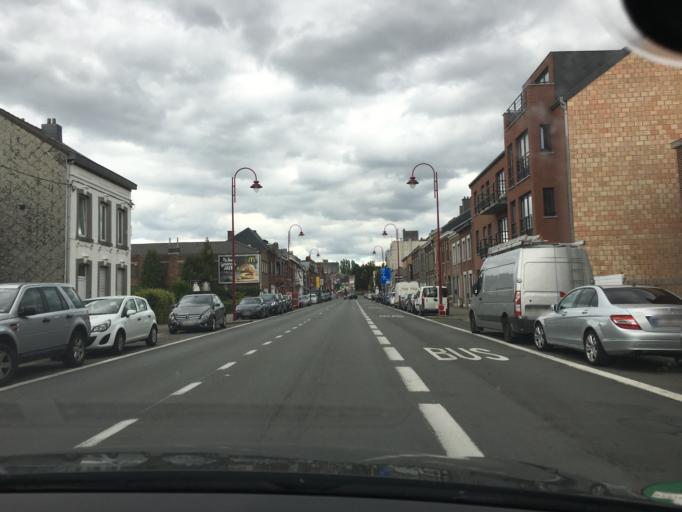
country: BE
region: Wallonia
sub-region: Province de Liege
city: Fleron
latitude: 50.6155
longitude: 5.6752
